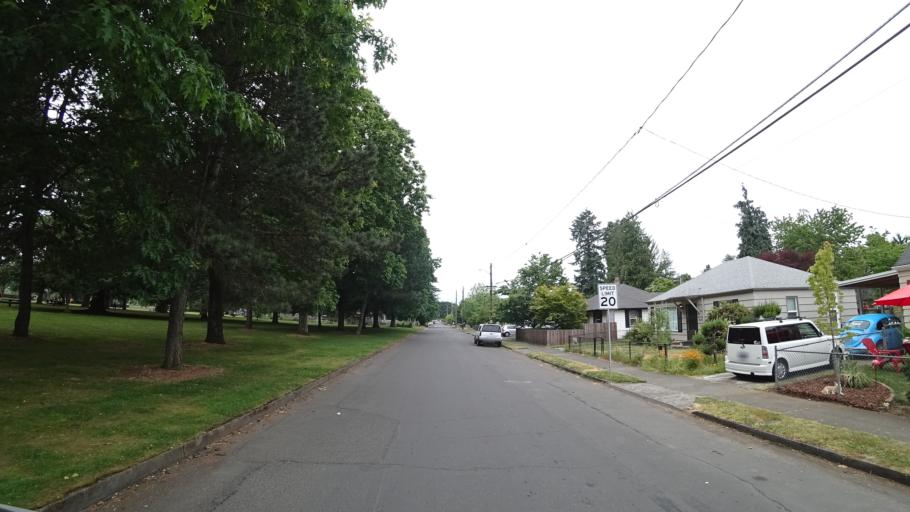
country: US
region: Oregon
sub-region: Multnomah County
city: Lents
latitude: 45.5155
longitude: -122.5694
